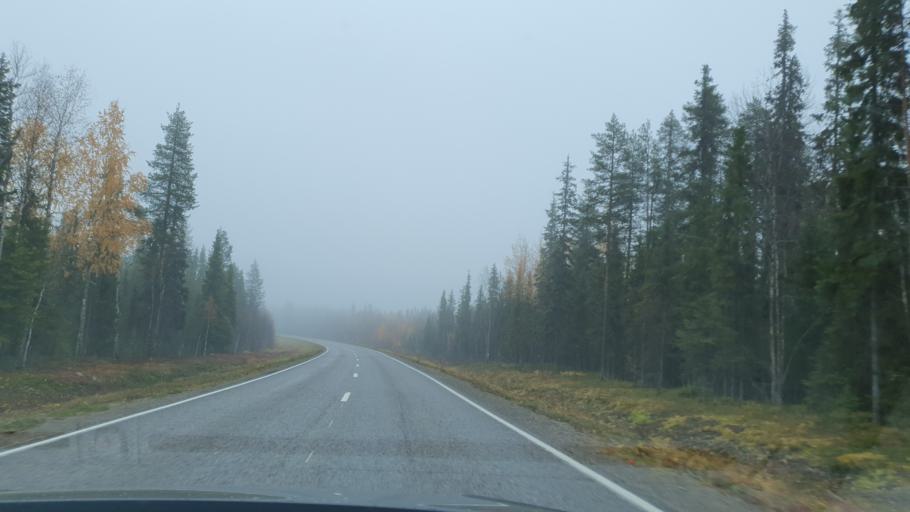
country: FI
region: Lapland
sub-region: Tunturi-Lappi
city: Kittilae
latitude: 67.6611
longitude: 24.8225
